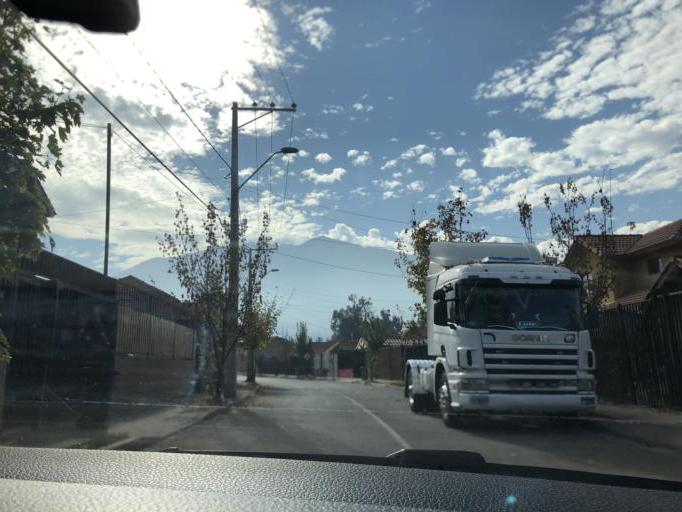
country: CL
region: Santiago Metropolitan
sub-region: Provincia de Cordillera
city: Puente Alto
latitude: -33.5886
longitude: -70.5312
